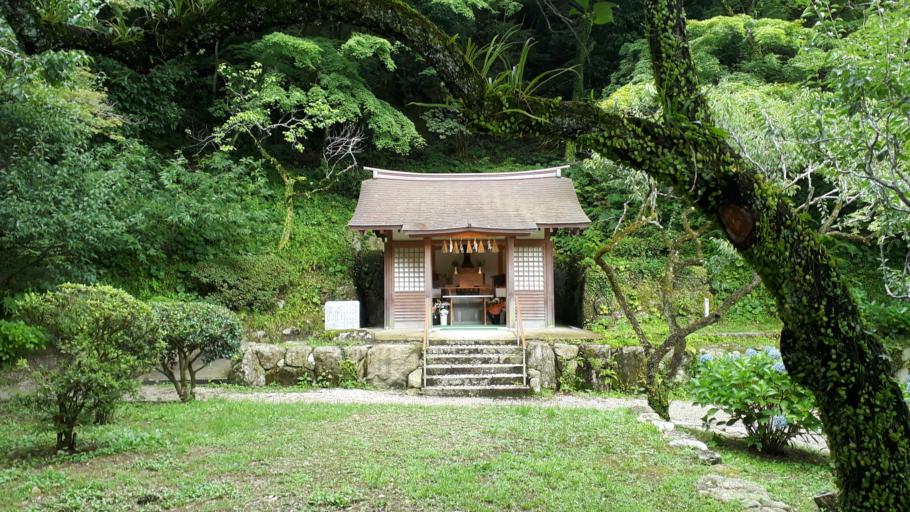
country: JP
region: Fukuoka
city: Dazaifu
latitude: 33.5225
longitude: 130.5347
